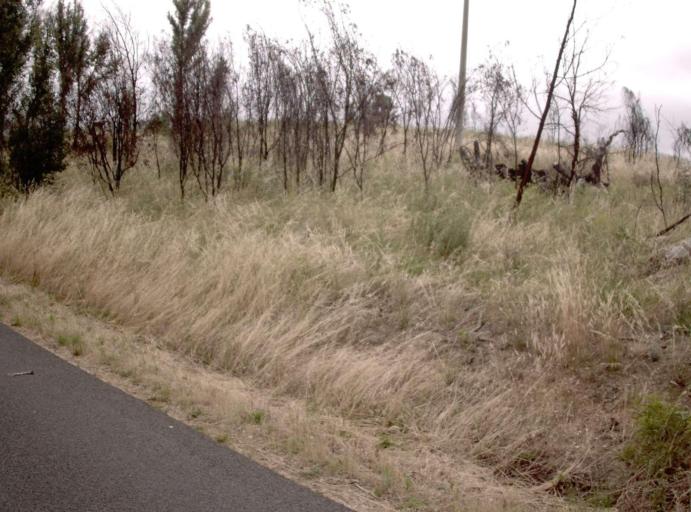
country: AU
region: Victoria
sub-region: Wellington
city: Heyfield
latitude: -37.8280
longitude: 146.6776
